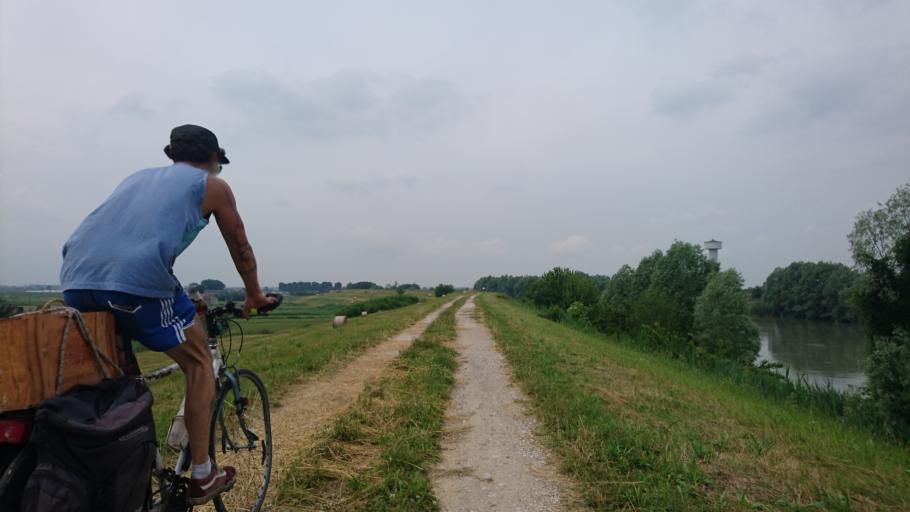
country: IT
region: Veneto
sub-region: Provincia di Padova
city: Piacenza d'Adige
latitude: 45.1211
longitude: 11.5667
